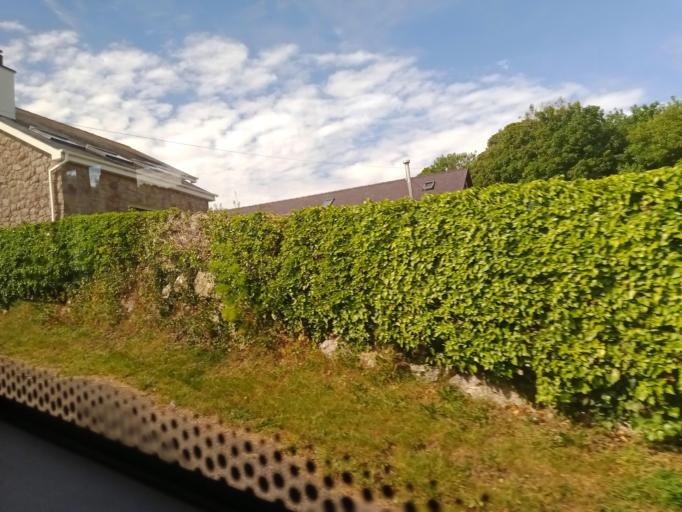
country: GB
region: Wales
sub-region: Anglesey
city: Llangoed
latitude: 53.2989
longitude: -4.0727
